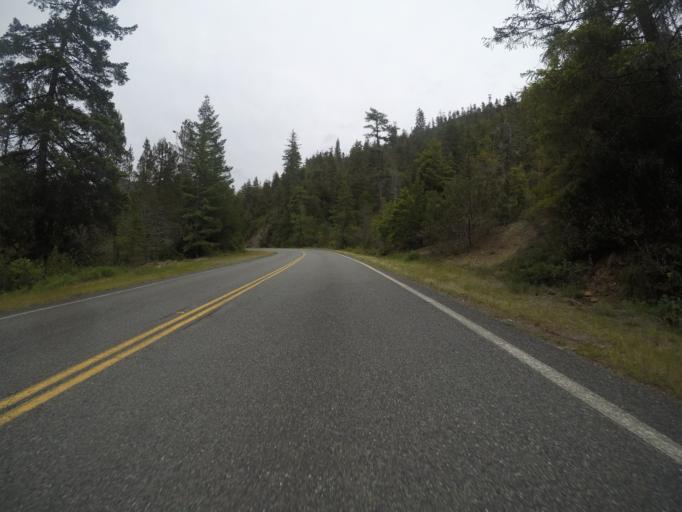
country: US
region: California
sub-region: Del Norte County
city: Bertsch-Oceanview
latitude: 41.7594
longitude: -124.0059
